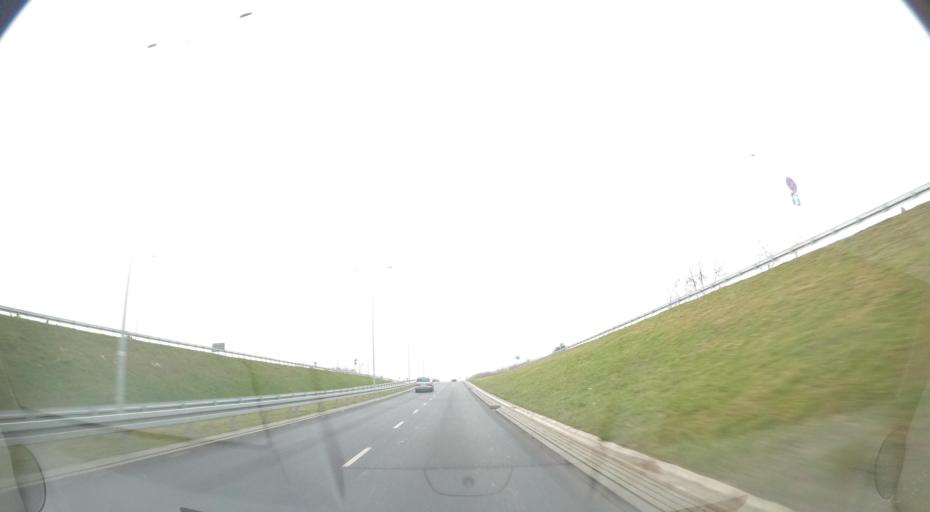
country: PL
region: Masovian Voivodeship
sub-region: Radom
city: Radom
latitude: 51.3964
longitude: 21.1969
